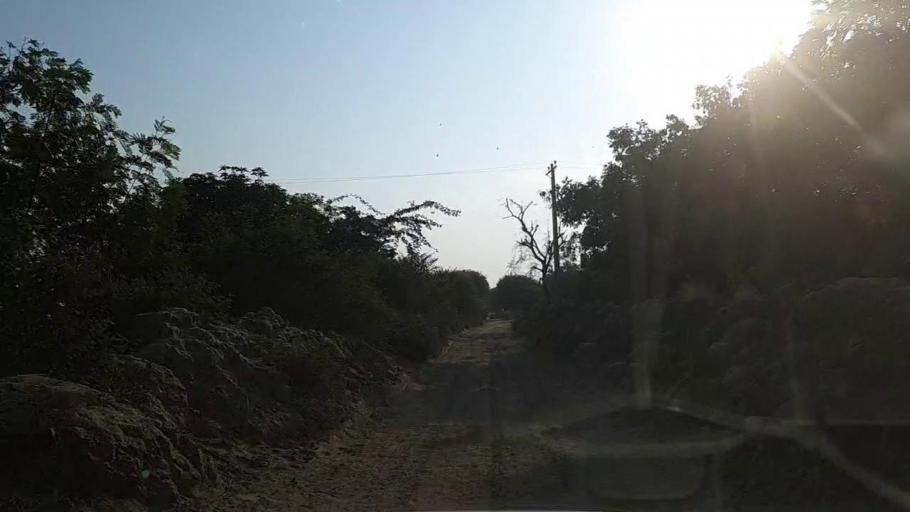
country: PK
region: Sindh
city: Mirpur Batoro
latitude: 24.7752
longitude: 68.2387
